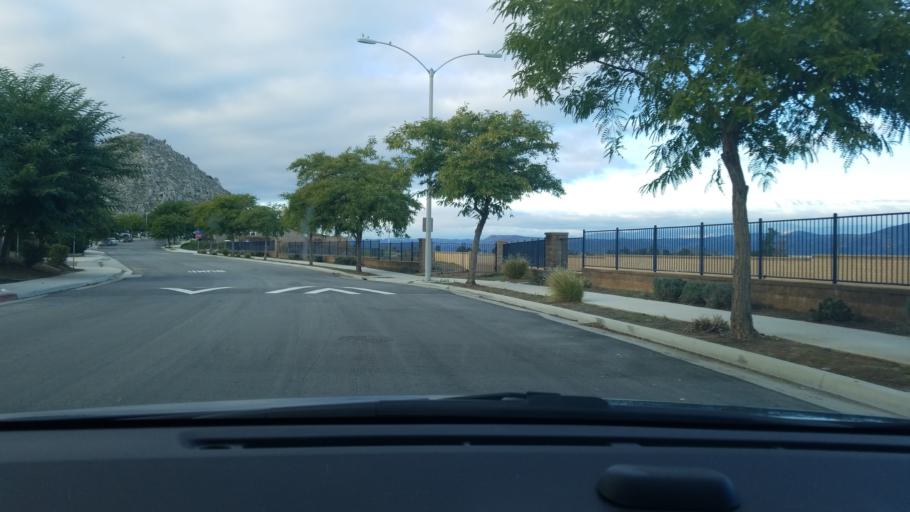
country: US
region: California
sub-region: Riverside County
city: Green Acres
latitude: 33.7963
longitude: -117.0356
